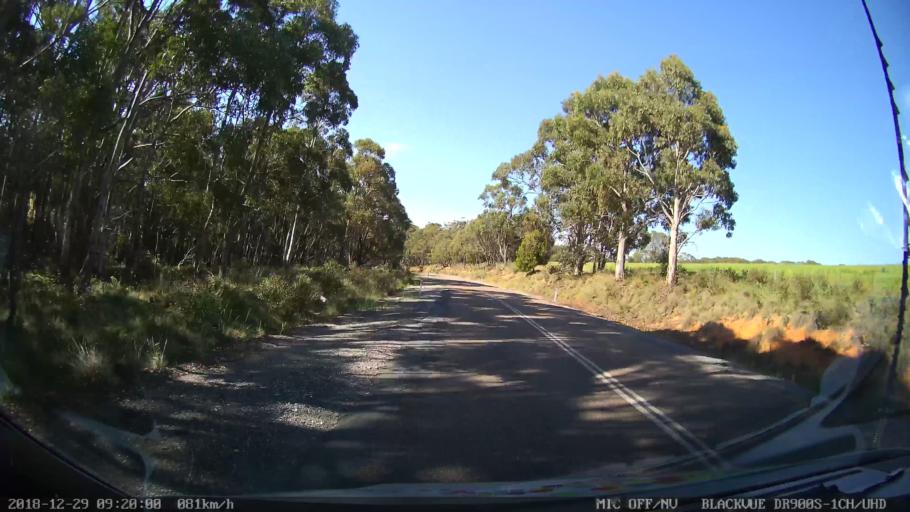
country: AU
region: New South Wales
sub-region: Upper Lachlan Shire
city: Crookwell
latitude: -34.4869
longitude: 149.4246
